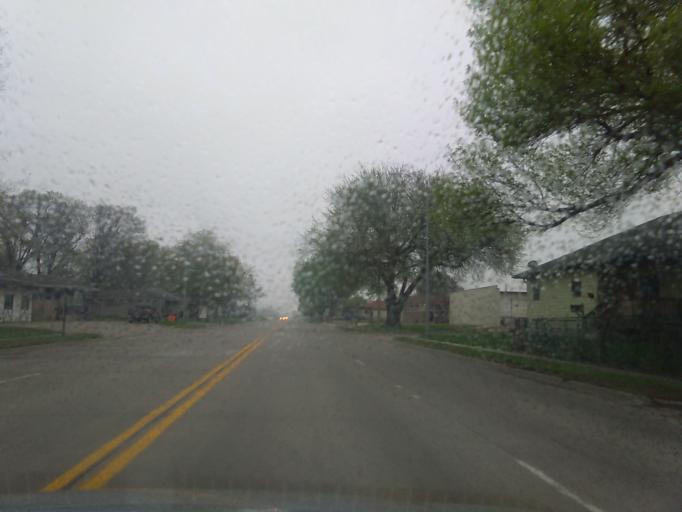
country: US
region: Nebraska
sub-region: Madison County
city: Norfolk
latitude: 42.0404
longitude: -97.4070
